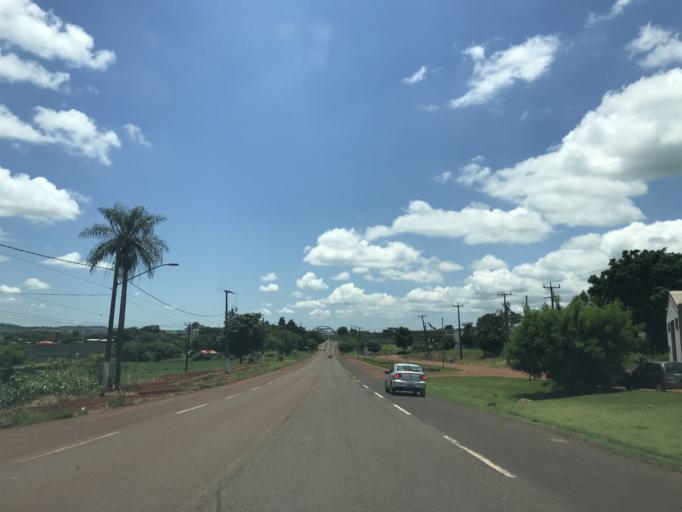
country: BR
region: Parana
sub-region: Marialva
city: Marialva
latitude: -23.4977
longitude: -51.7760
